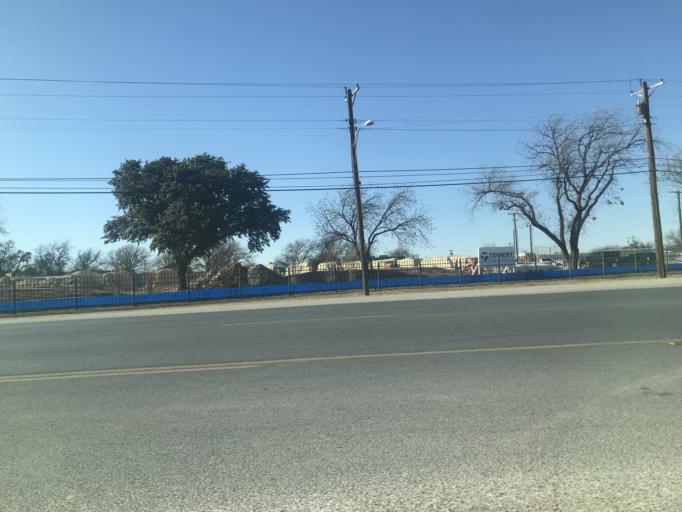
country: US
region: Texas
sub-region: Taylor County
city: Abilene
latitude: 32.4166
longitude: -99.7423
